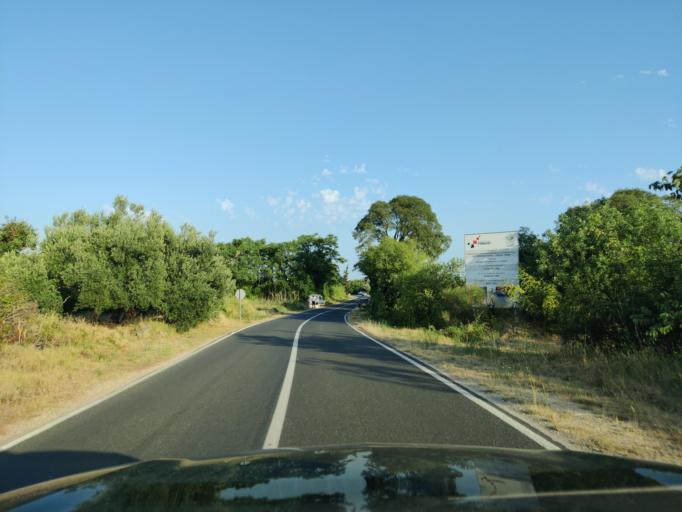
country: HR
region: Sibensko-Kniniska
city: Tribunj
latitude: 43.7711
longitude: 15.7270
